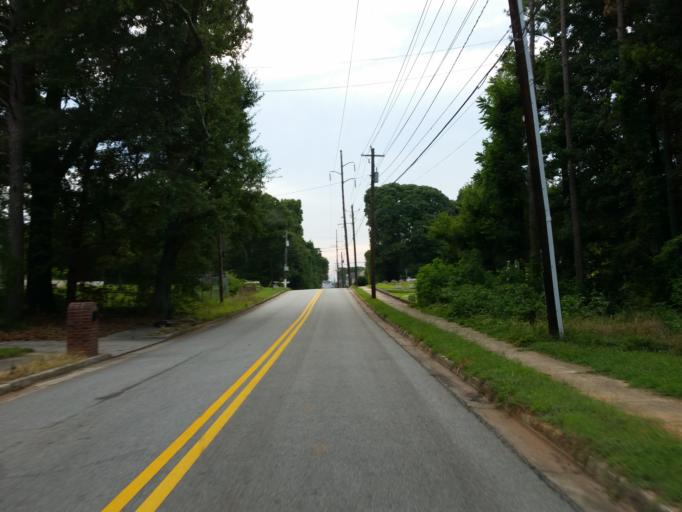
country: US
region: Georgia
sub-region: Cobb County
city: Smyrna
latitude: 33.8906
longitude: -84.5080
